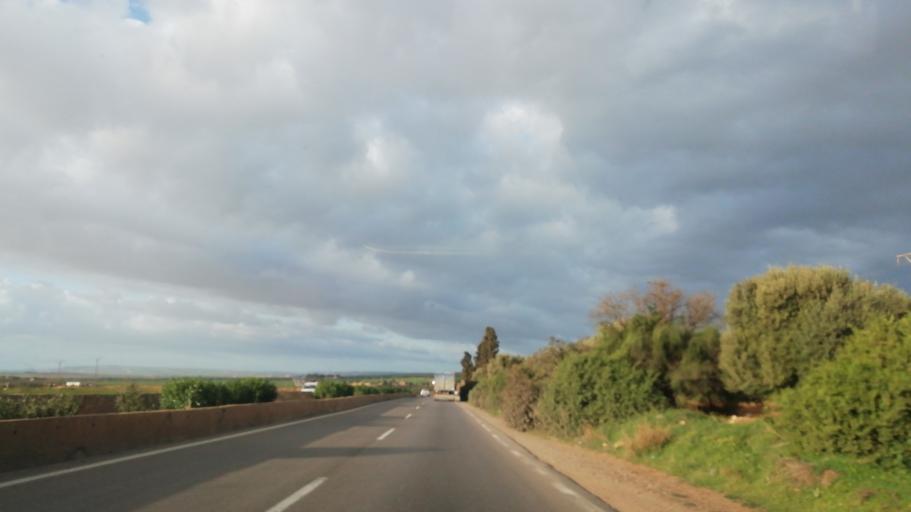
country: DZ
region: Oran
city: Bou Tlelis
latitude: 35.5555
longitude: -0.9422
